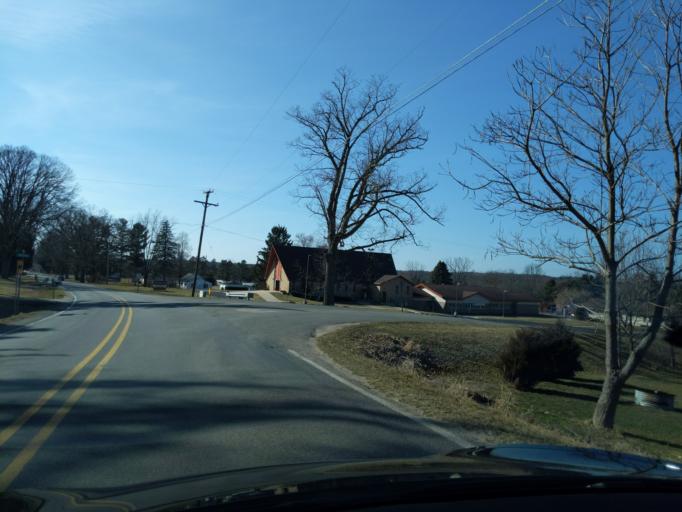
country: US
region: Michigan
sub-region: Ionia County
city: Saranac
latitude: 42.9298
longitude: -85.1939
